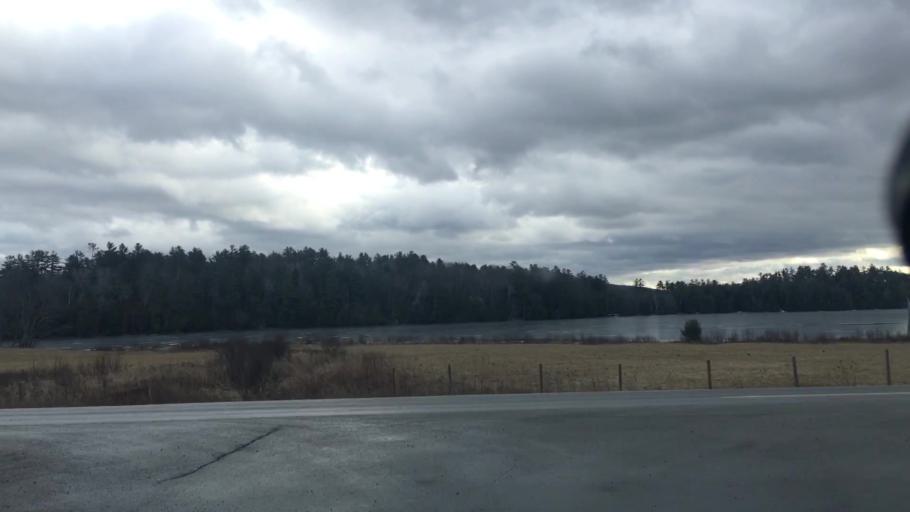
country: US
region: Maine
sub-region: Hancock County
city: Orland
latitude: 44.6300
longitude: -68.7056
